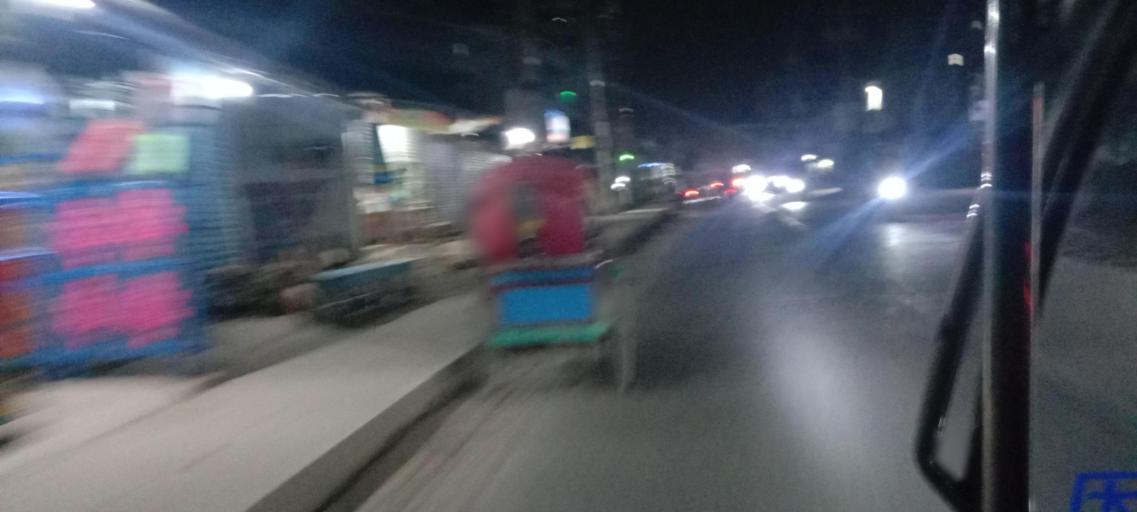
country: BD
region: Dhaka
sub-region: Dhaka
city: Dhaka
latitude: 23.7002
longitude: 90.3835
